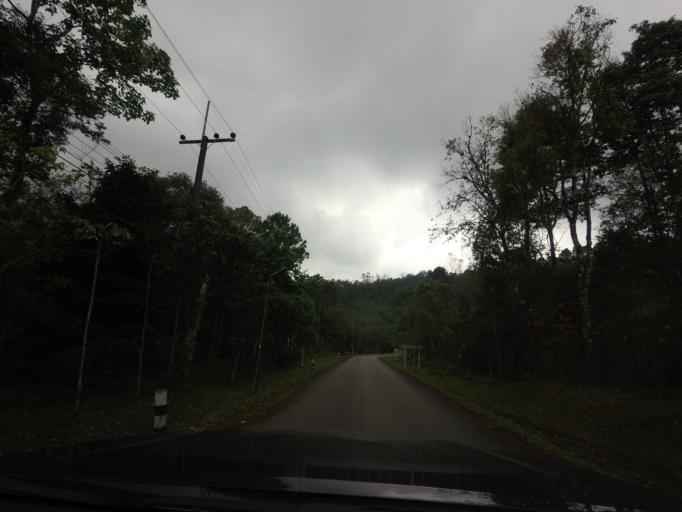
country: TH
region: Nan
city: Bo Kluea
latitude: 19.1994
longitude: 101.0809
